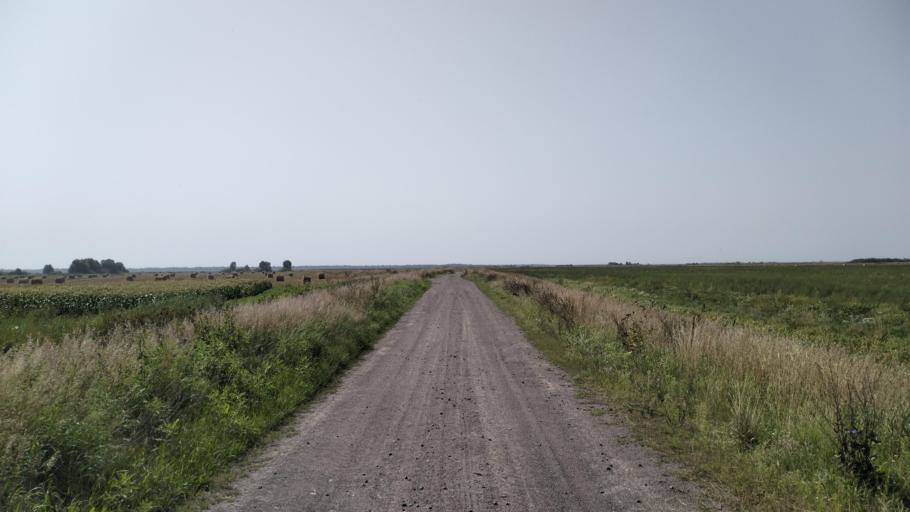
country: BY
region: Brest
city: Davyd-Haradok
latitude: 52.0050
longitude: 27.1661
